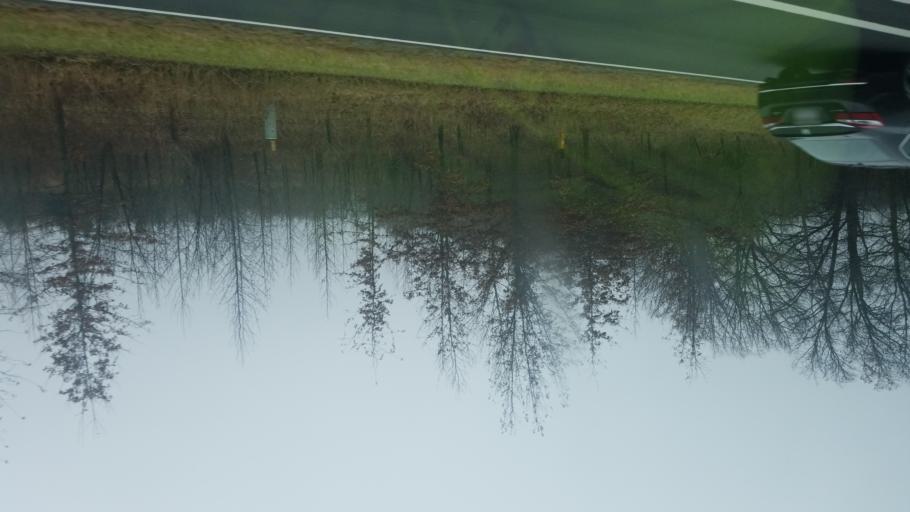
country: US
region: Ohio
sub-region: Union County
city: Marysville
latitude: 40.2489
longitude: -83.4180
